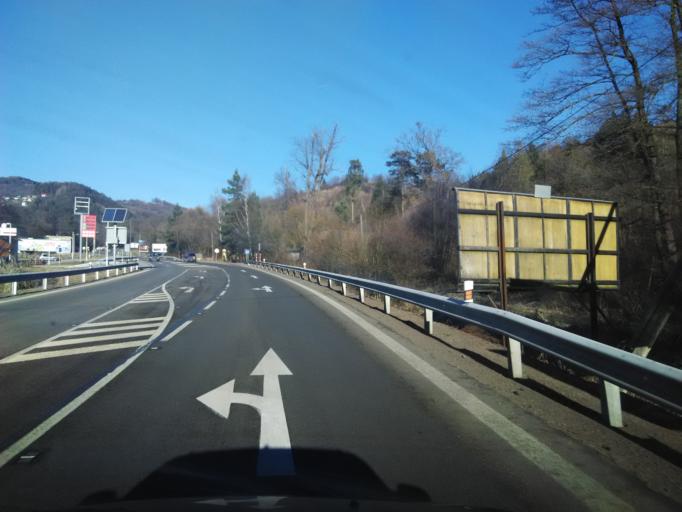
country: SK
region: Banskobystricky
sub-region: Okres Ziar nad Hronom
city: Kremnica
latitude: 48.6854
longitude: 18.9186
